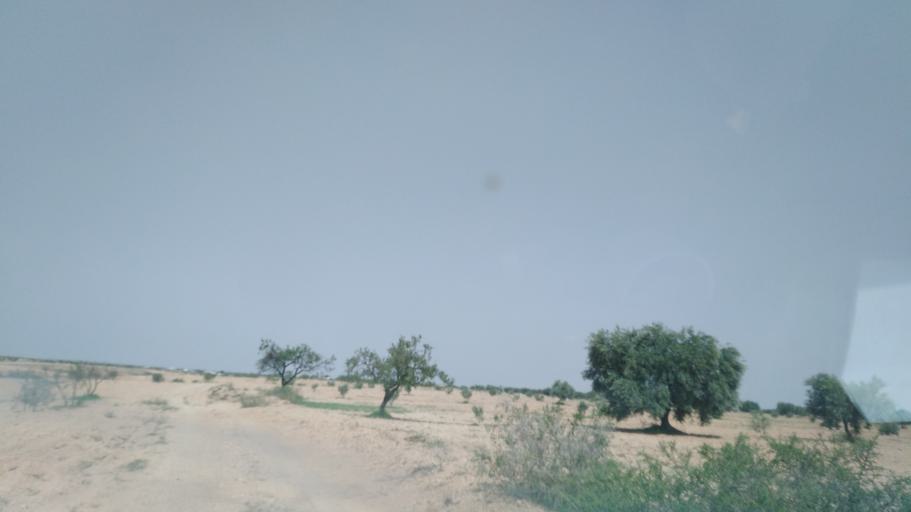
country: TN
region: Safaqis
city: Sfax
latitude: 34.6480
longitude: 10.5581
